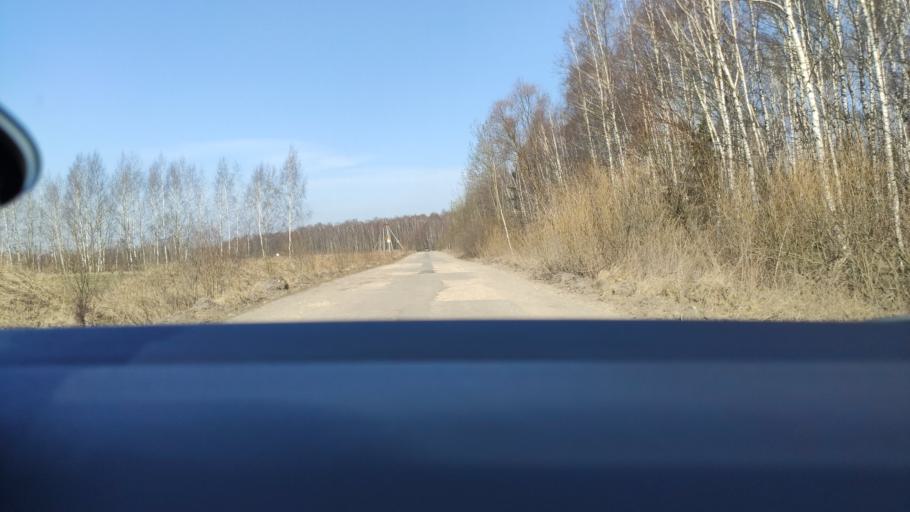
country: RU
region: Moskovskaya
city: Elektrostal'
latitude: 55.7712
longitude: 38.3823
